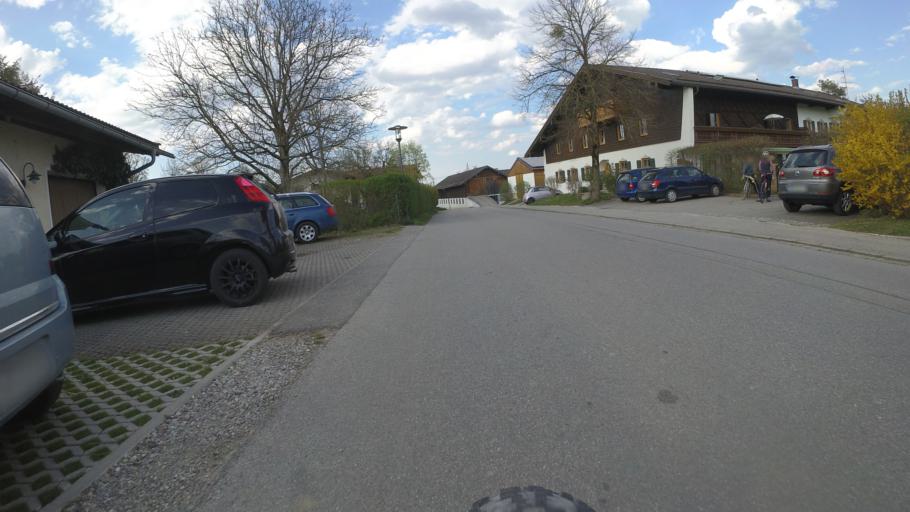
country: DE
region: Bavaria
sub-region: Upper Bavaria
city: Seeon-Seebruck
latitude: 47.9367
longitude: 12.4778
